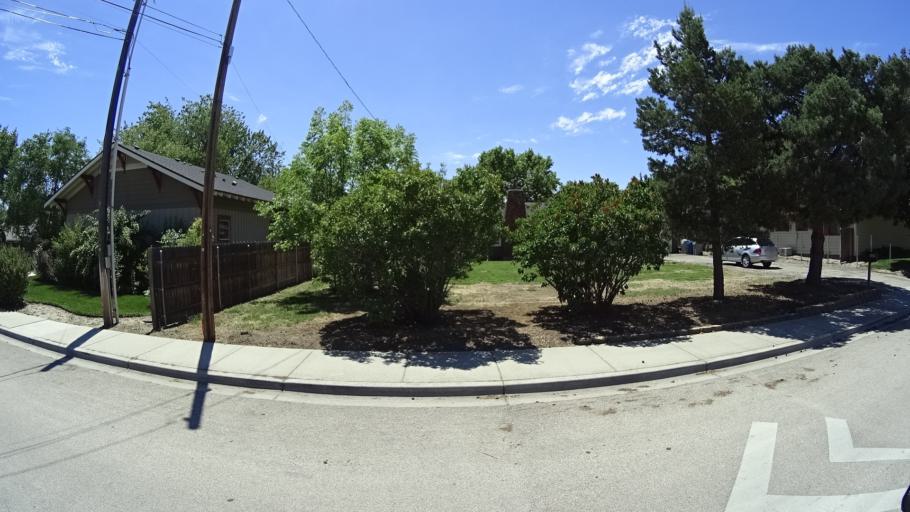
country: US
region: Idaho
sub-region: Ada County
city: Garden City
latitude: 43.5988
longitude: -116.2356
